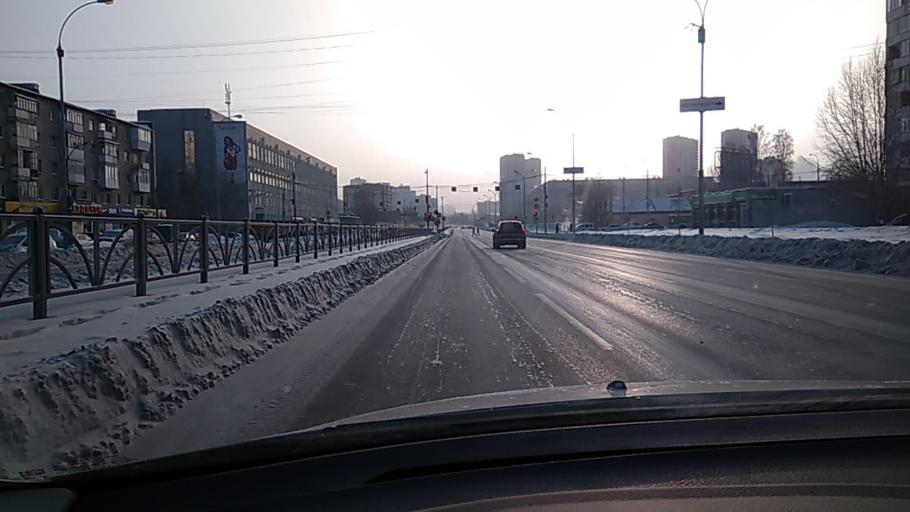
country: RU
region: Sverdlovsk
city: Yekaterinburg
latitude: 56.8117
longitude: 60.6294
